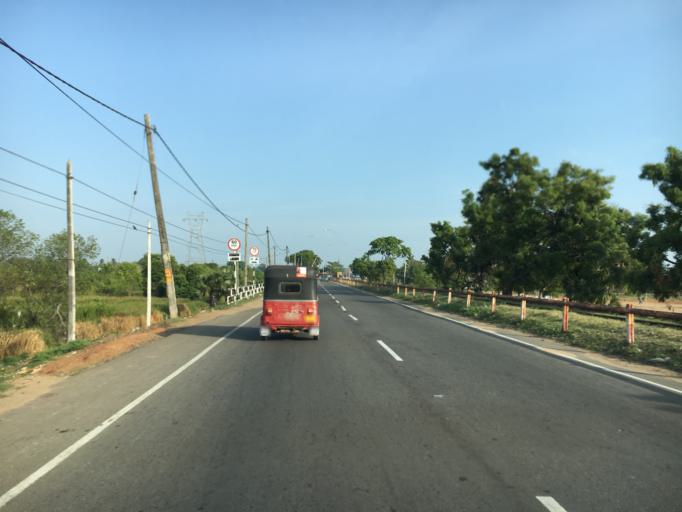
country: LK
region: Eastern Province
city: Eravur Town
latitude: 7.9185
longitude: 81.5181
